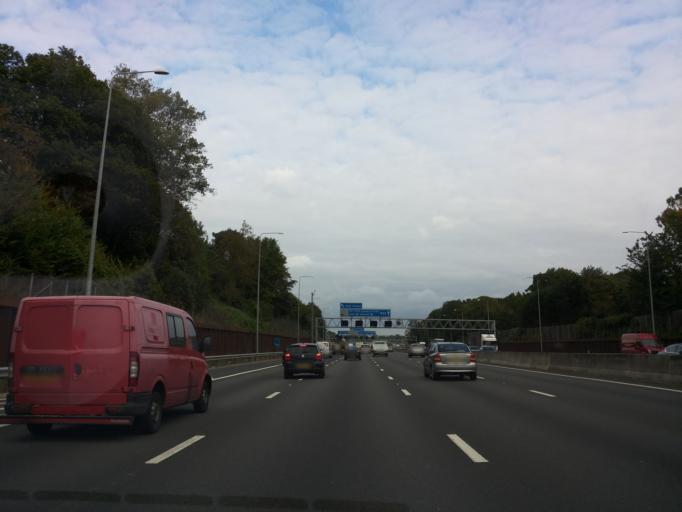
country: GB
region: England
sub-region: Hertfordshire
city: Chorleywood
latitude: 51.6759
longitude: -0.4610
